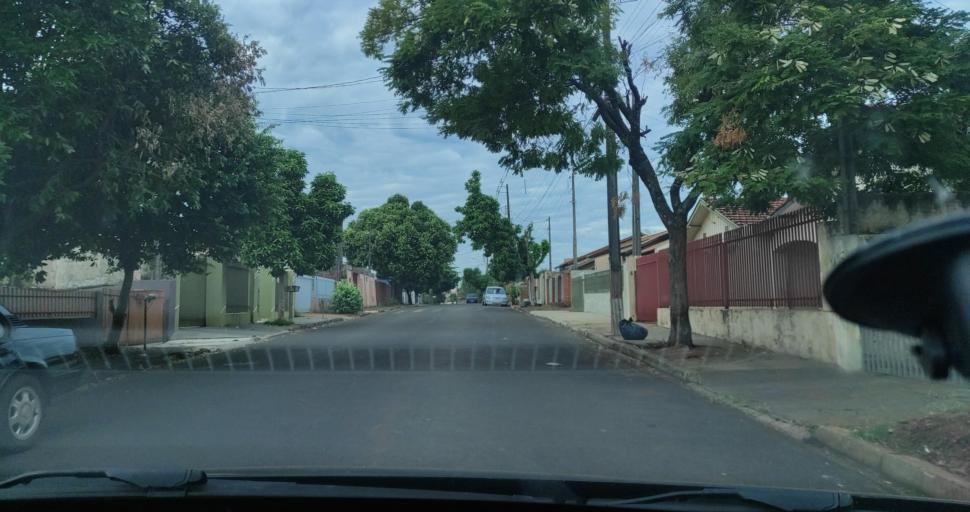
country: BR
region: Parana
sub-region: Ibipora
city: Ibipora
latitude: -23.2579
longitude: -51.0484
